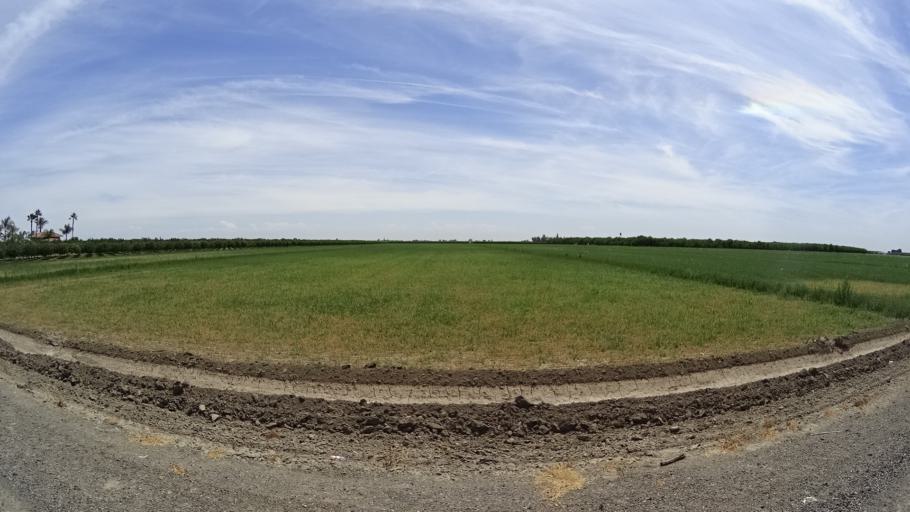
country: US
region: California
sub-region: Kings County
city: Lucerne
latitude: 36.3841
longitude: -119.6910
